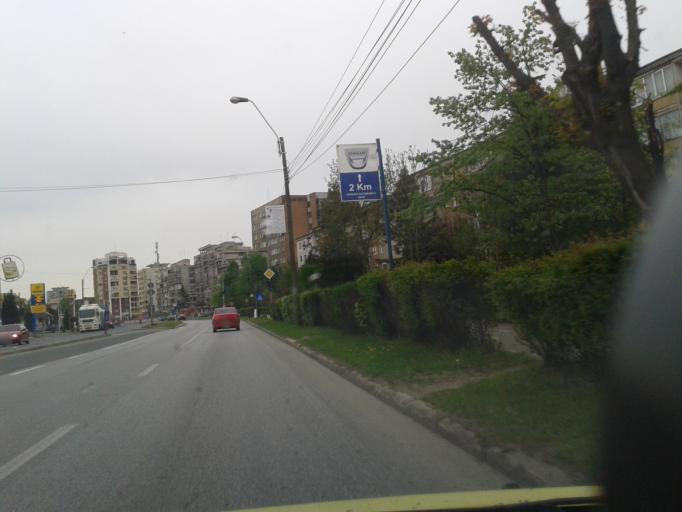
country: RO
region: Hunedoara
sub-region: Municipiul Deva
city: Deva
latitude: 45.8855
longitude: 22.9079
